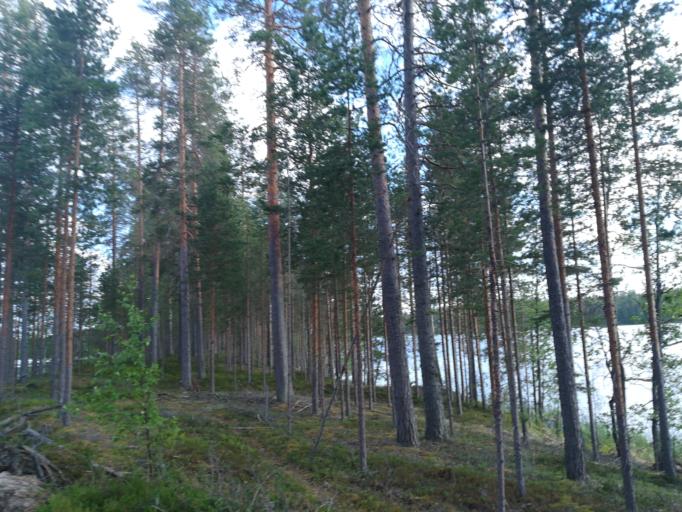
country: FI
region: Southern Savonia
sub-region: Savonlinna
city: Savonlinna
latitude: 61.6425
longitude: 28.7122
